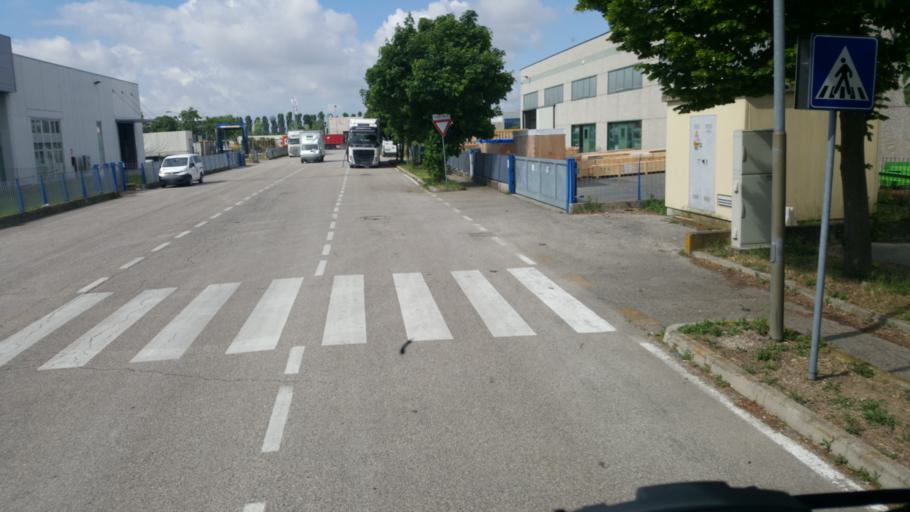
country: IT
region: Veneto
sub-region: Provincia di Venezia
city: Noventa di Piave
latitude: 45.6739
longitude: 12.5595
